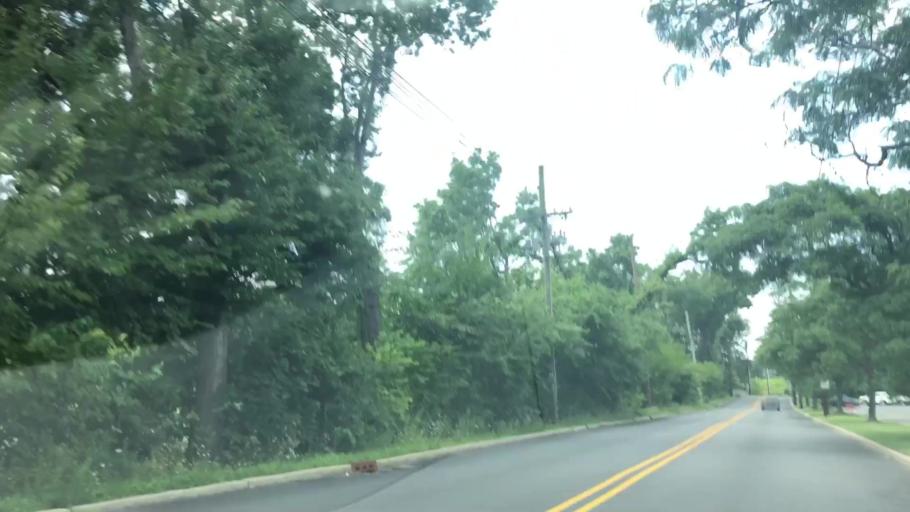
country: US
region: New Jersey
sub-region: Bergen County
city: Rochelle Park
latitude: 40.9131
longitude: -74.0764
